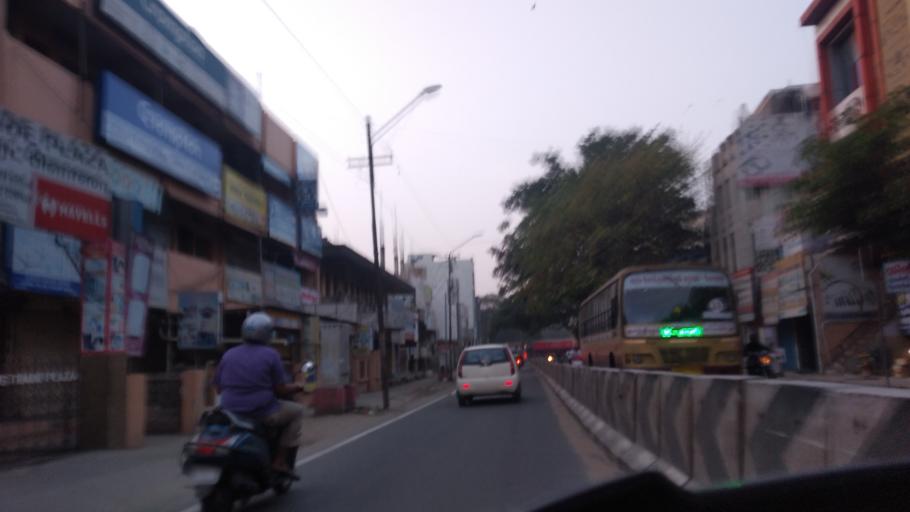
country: IN
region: Tamil Nadu
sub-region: Coimbatore
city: Coimbatore
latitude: 11.0036
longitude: 76.9665
